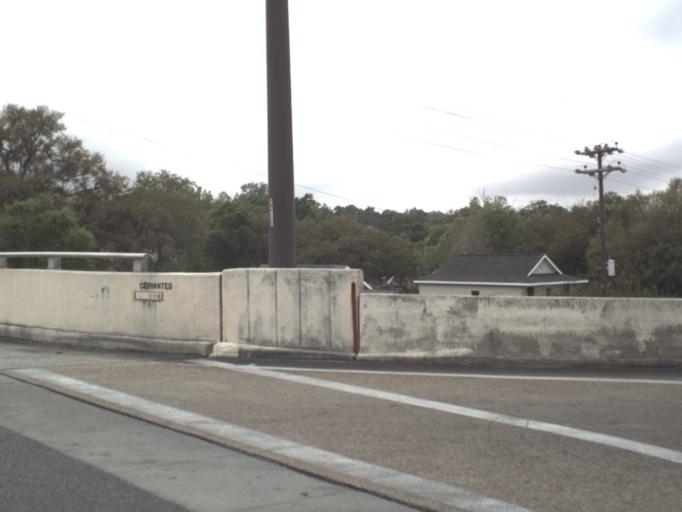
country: US
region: Florida
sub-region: Escambia County
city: Pensacola
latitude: 30.4219
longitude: -87.2144
